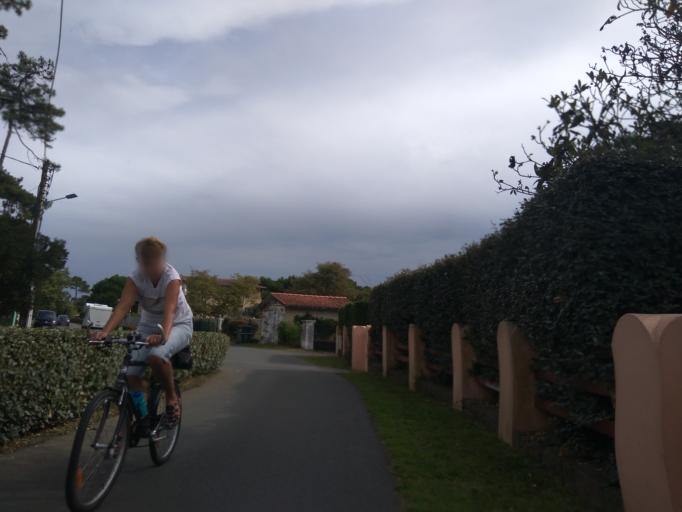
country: FR
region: Aquitaine
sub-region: Departement des Landes
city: Capbreton
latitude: 43.6401
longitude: -1.4401
